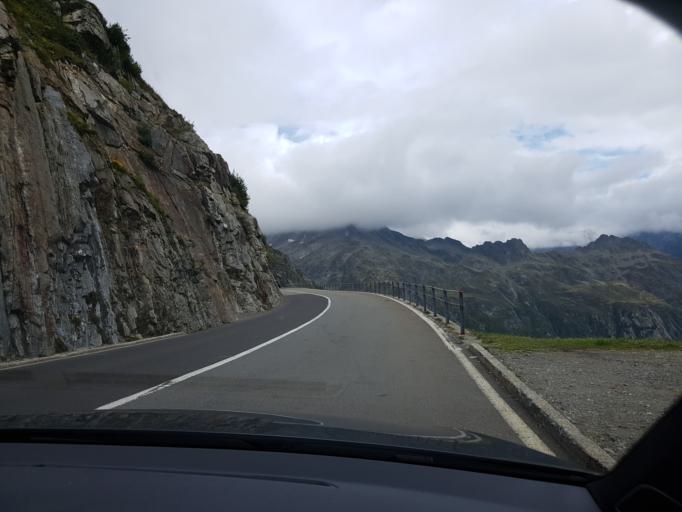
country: CH
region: Obwalden
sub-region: Obwalden
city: Engelberg
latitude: 46.7334
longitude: 8.4542
